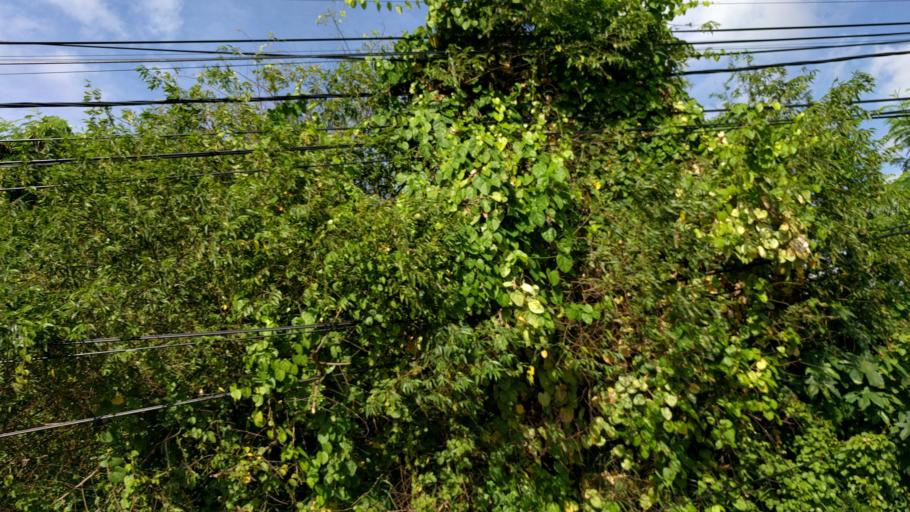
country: ID
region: Bali
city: Kuta
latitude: -8.6978
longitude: 115.1769
